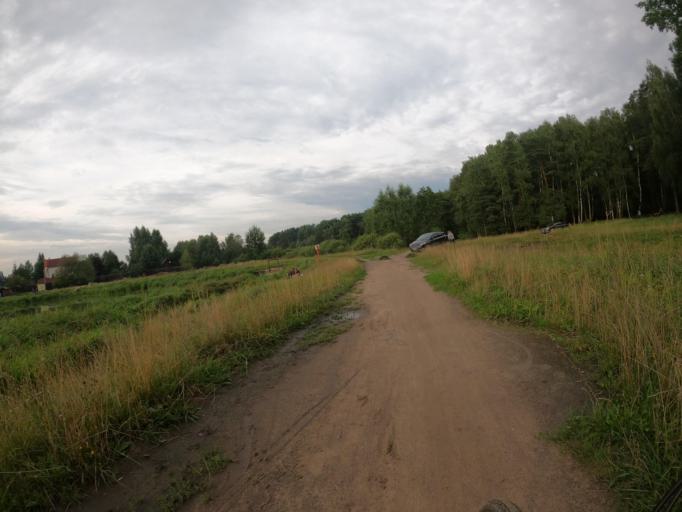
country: RU
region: Moskovskaya
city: Bykovo
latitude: 55.6516
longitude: 38.1097
